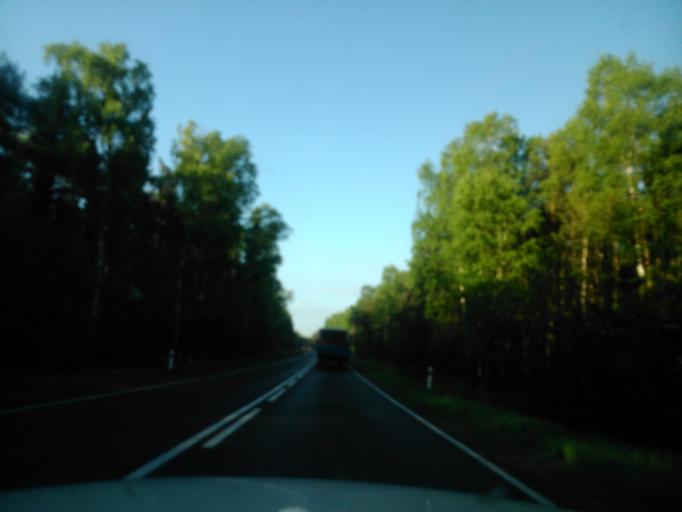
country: PL
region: Masovian Voivodeship
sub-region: Powiat sochaczewski
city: Mlodzieszyn
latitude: 52.3263
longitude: 20.2120
